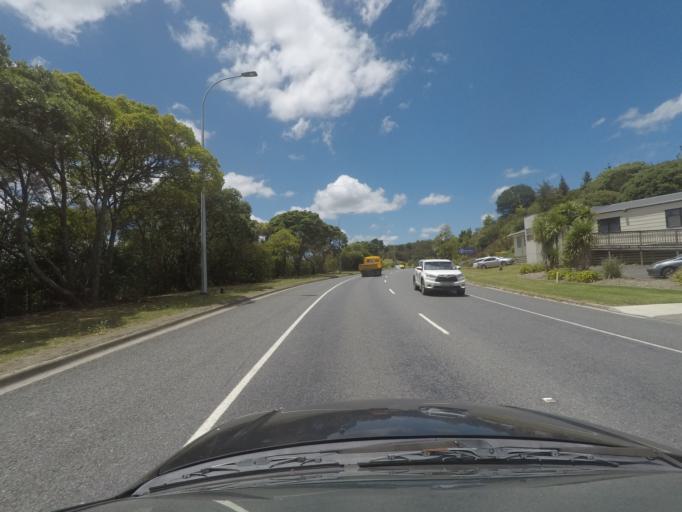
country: NZ
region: Northland
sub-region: Whangarei
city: Whangarei
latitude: -35.7443
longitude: 174.3256
